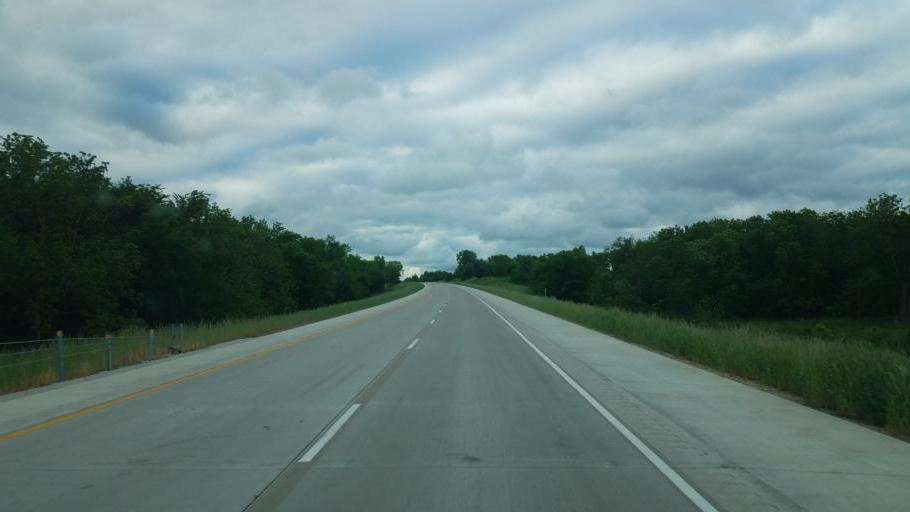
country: US
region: Iowa
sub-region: Decatur County
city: Lamoni
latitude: 40.5979
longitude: -93.9109
